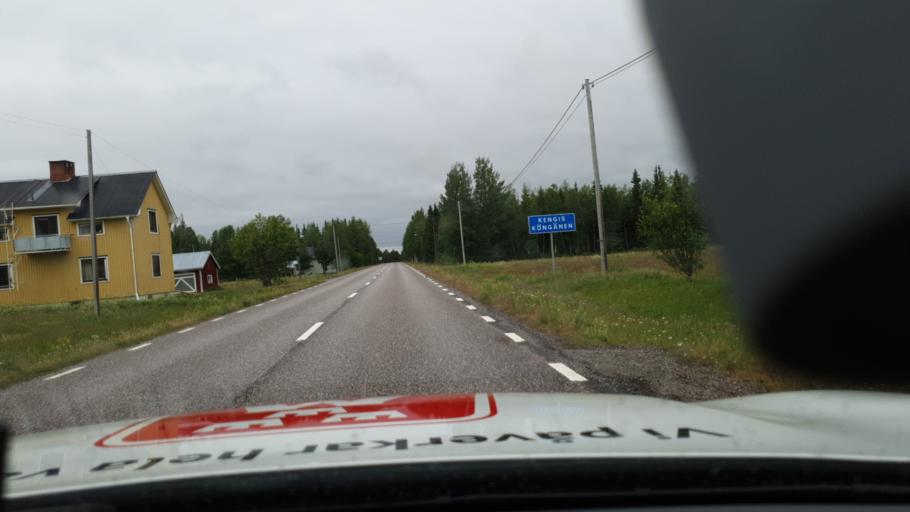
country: SE
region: Norrbotten
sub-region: Pajala Kommun
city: Pajala
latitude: 67.1907
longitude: 23.4726
